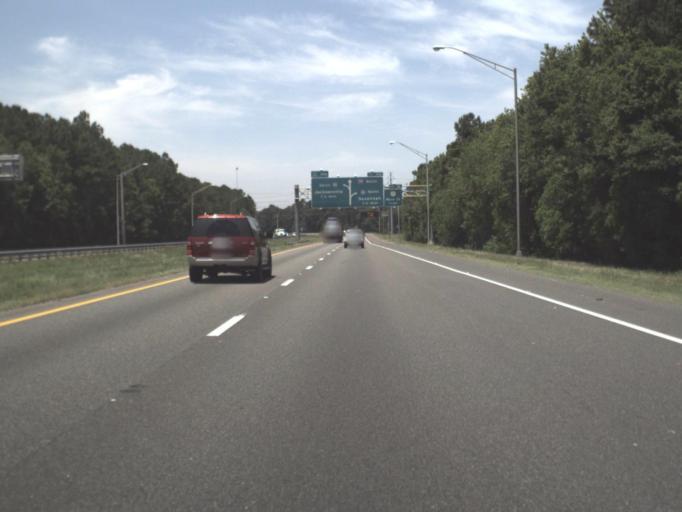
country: US
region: Florida
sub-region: Duval County
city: Jacksonville
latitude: 30.4522
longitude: -81.6190
